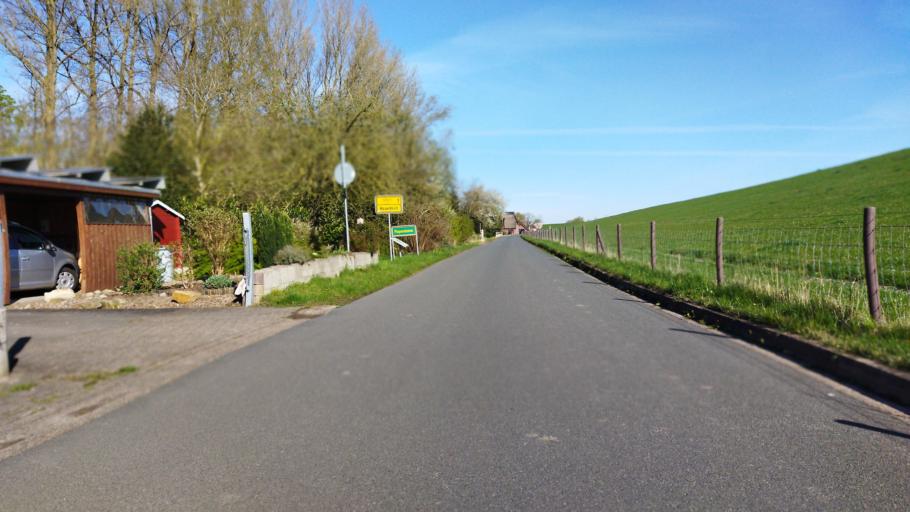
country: DE
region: Lower Saxony
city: Elsfleth
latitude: 53.2071
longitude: 8.4865
